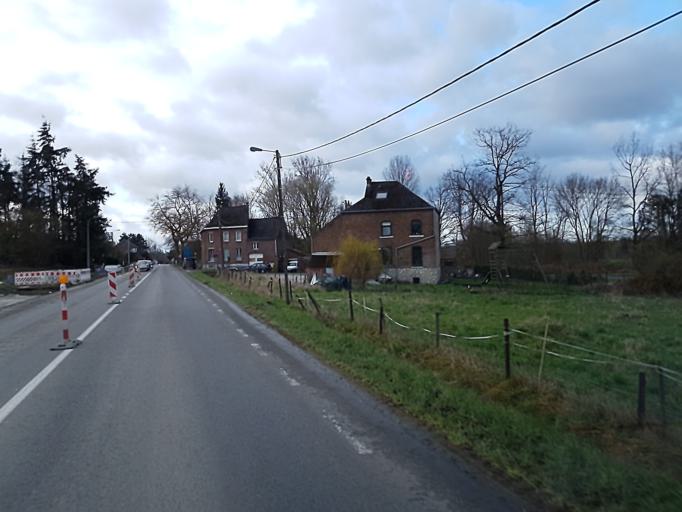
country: BE
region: Wallonia
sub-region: Province du Brabant Wallon
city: Jodoigne
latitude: 50.7403
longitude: 4.8802
